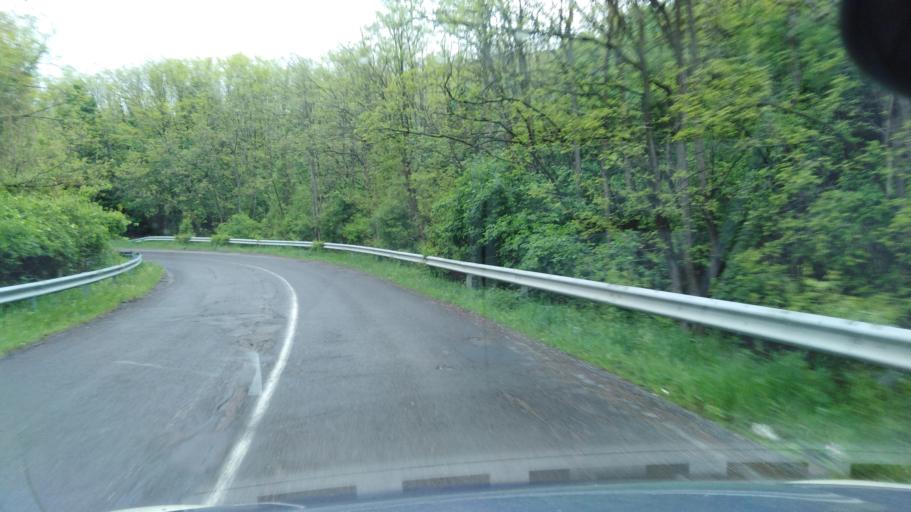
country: HU
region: Nograd
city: Rimoc
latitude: 48.0209
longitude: 19.5957
